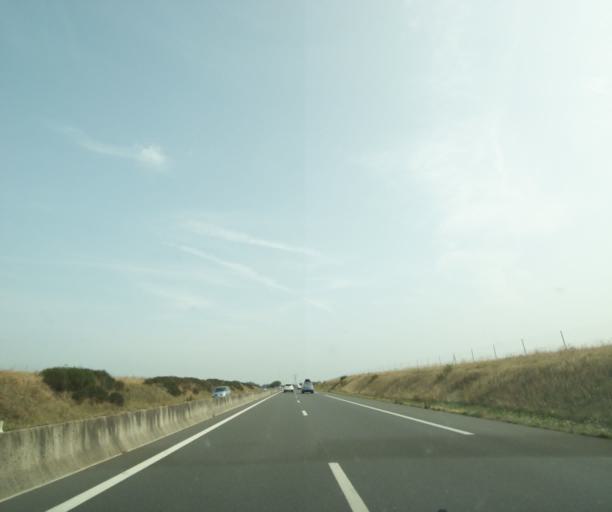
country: FR
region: Pays de la Loire
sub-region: Departement de la Sarthe
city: Arconnay
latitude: 48.3620
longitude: 0.0985
